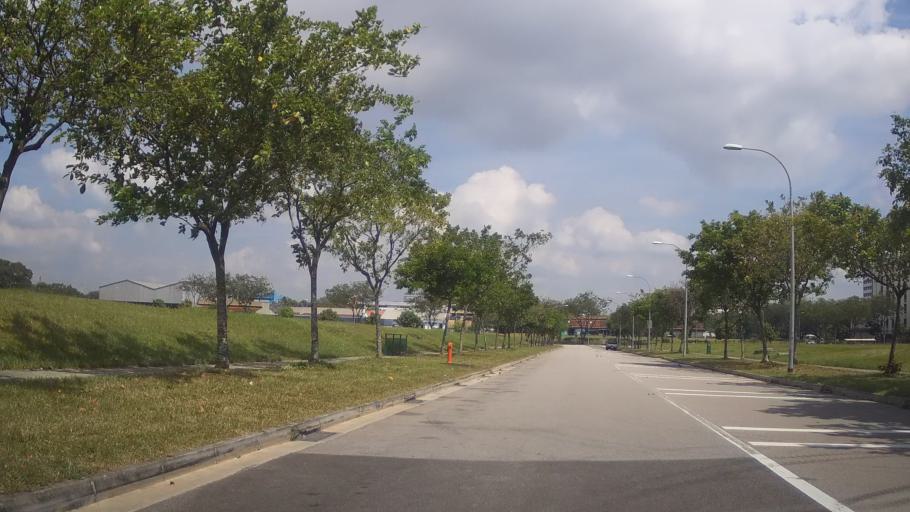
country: SG
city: Singapore
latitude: 1.3253
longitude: 103.7180
